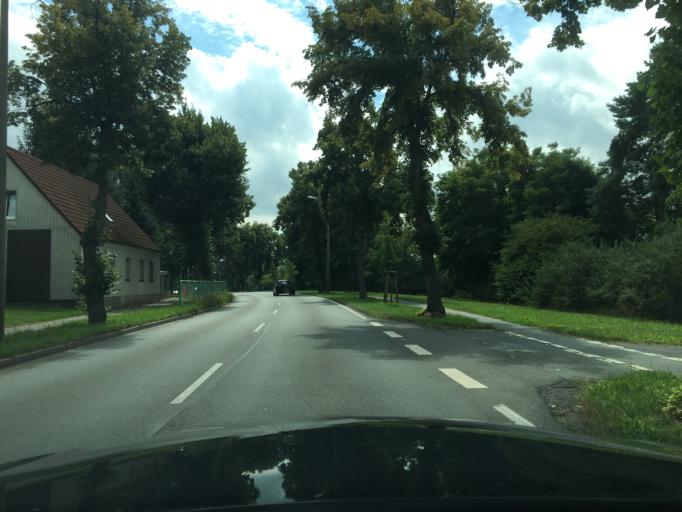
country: DE
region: Saxony-Anhalt
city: Bobbau
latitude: 51.6738
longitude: 12.2750
